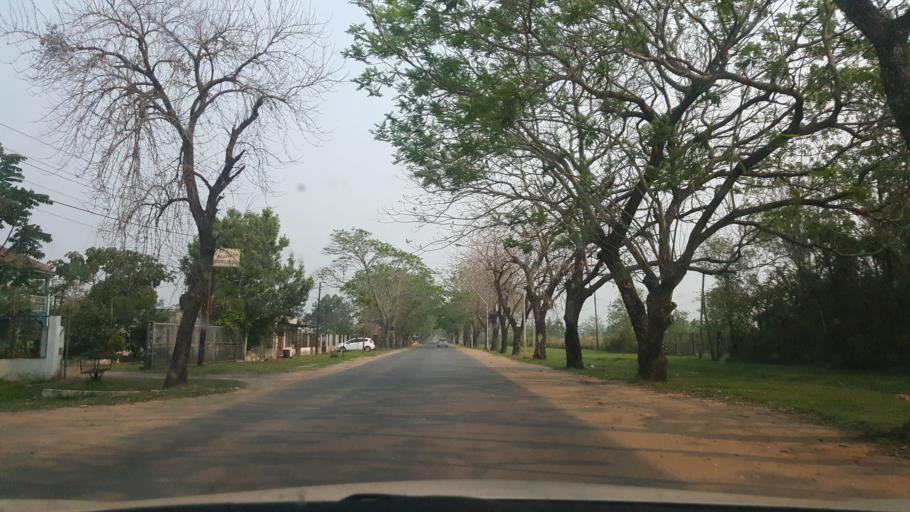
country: AR
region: Corrientes
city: Ita Ibate
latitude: -27.4309
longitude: -57.3385
